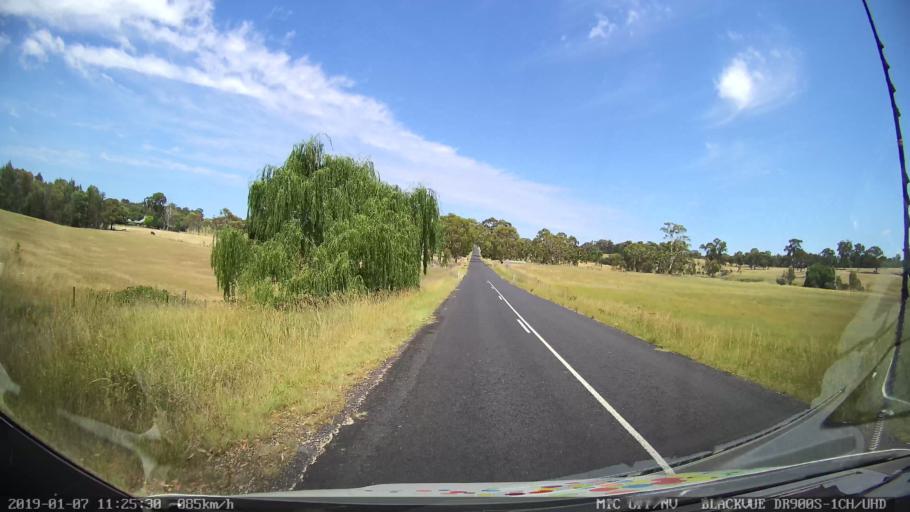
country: AU
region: New South Wales
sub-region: Armidale Dumaresq
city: Armidale
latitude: -30.4603
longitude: 151.6006
